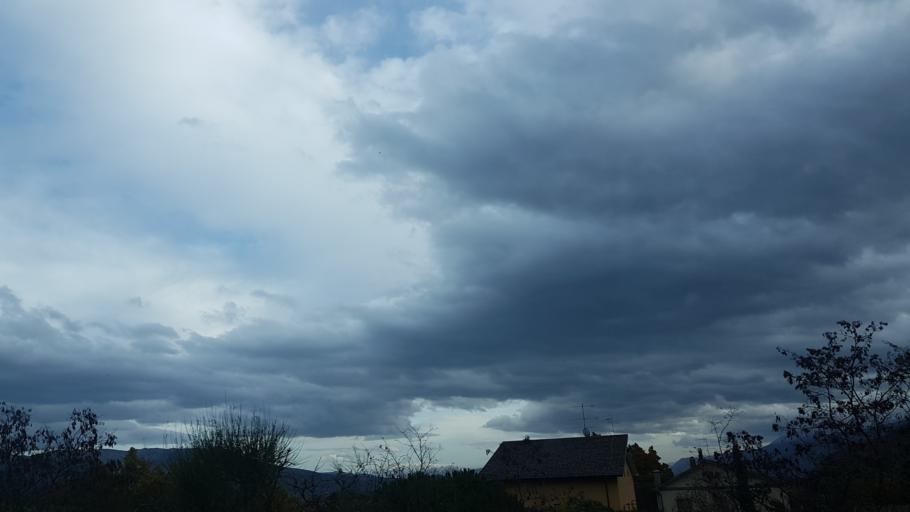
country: IT
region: Abruzzo
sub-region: Provincia dell' Aquila
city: Progetto Case Bazzano
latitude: 42.3658
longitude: 13.4291
